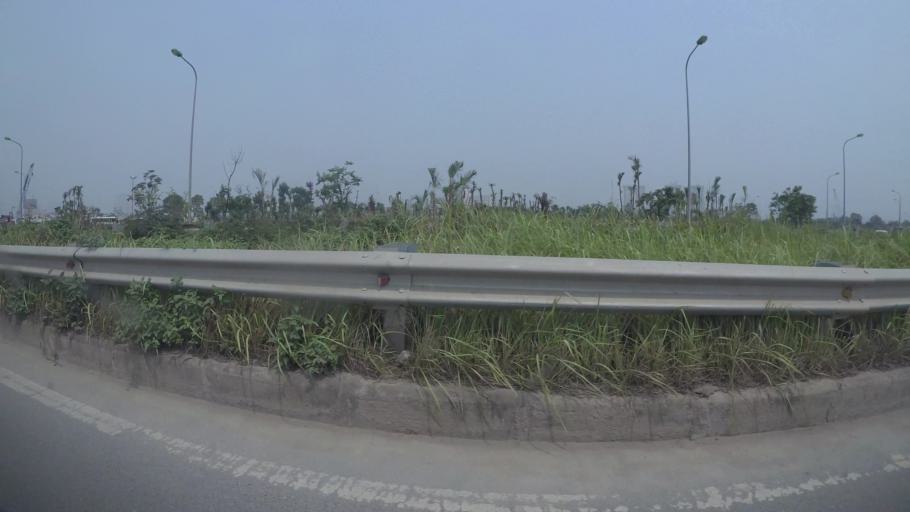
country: VN
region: Ha Noi
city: Cau Dien
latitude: 21.0070
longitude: 105.7498
